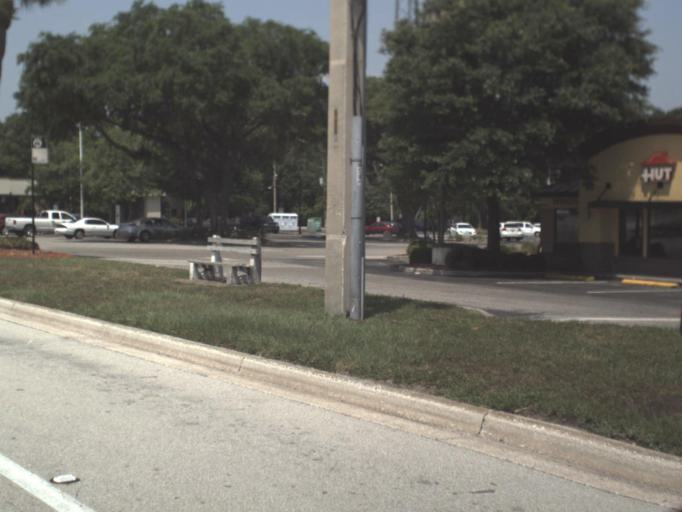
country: US
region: Florida
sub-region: Clay County
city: Bellair-Meadowbrook Terrace
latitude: 30.2934
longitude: -81.7798
